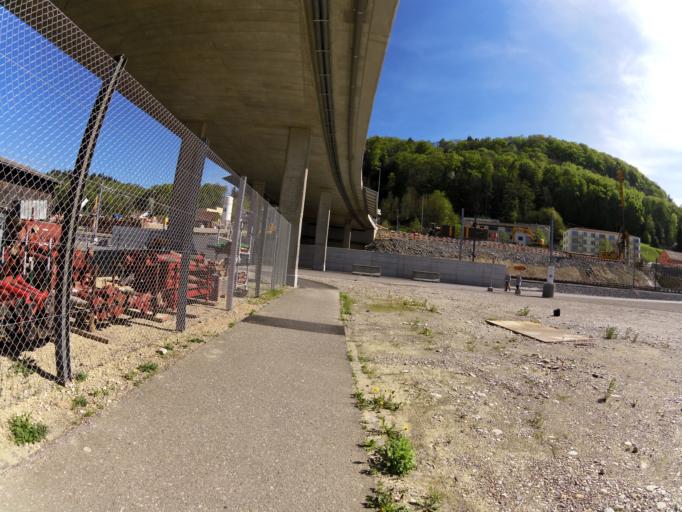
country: CH
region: Solothurn
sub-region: Bezirk Goesgen
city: Niedererlinsbach
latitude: 47.3844
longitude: 8.0240
